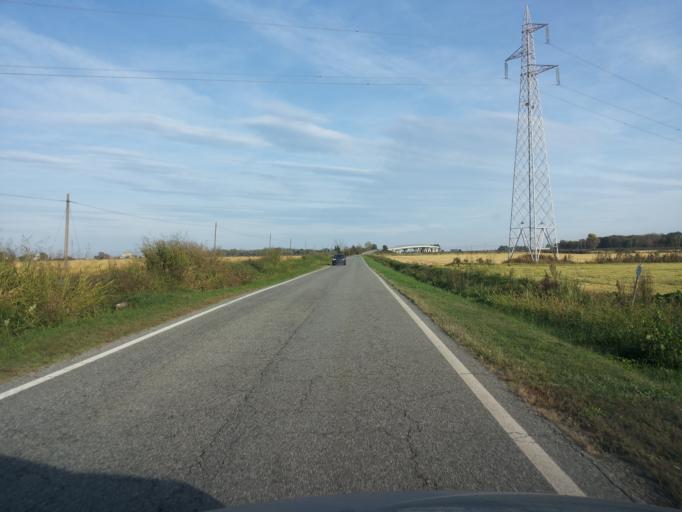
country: IT
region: Piedmont
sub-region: Provincia di Vercelli
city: Carisio
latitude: 45.4302
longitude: 8.1868
